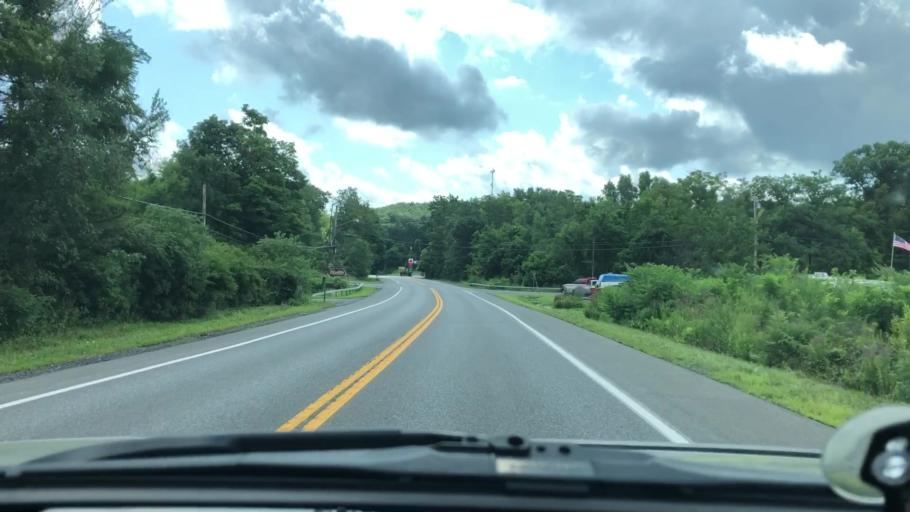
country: US
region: New York
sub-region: Ulster County
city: Manorville
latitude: 42.1209
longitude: -73.9920
